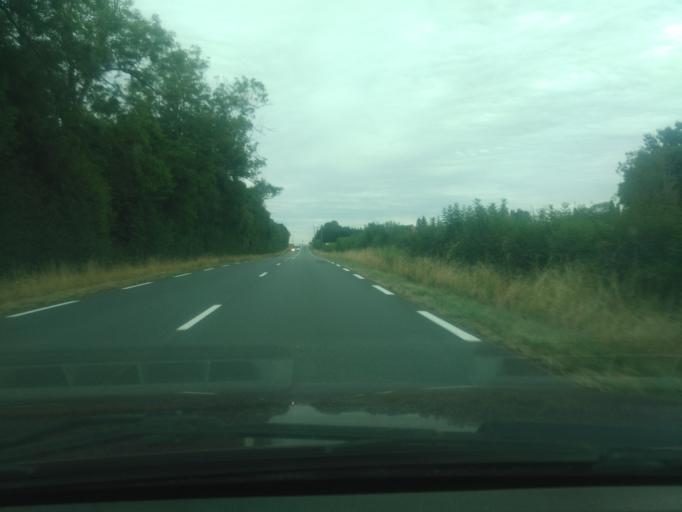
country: FR
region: Centre
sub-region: Departement de l'Indre
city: Neuvy-Saint-Sepulchre
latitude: 46.5988
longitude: 1.7675
